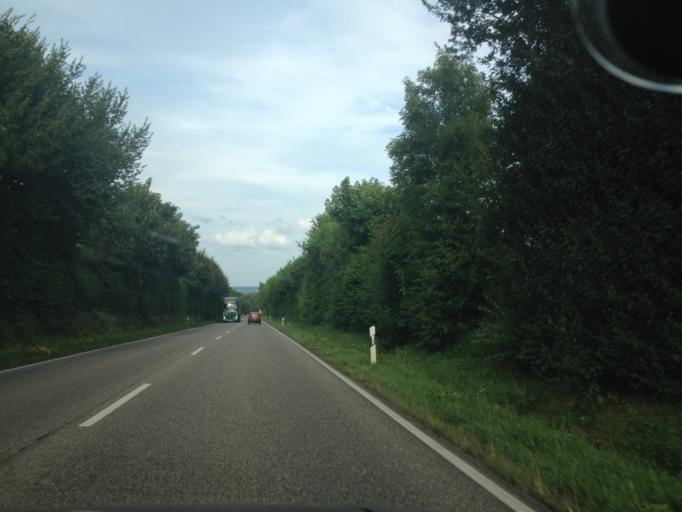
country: DE
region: Baden-Wuerttemberg
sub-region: Regierungsbezirk Stuttgart
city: Schwaigern
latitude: 49.1452
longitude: 9.0809
